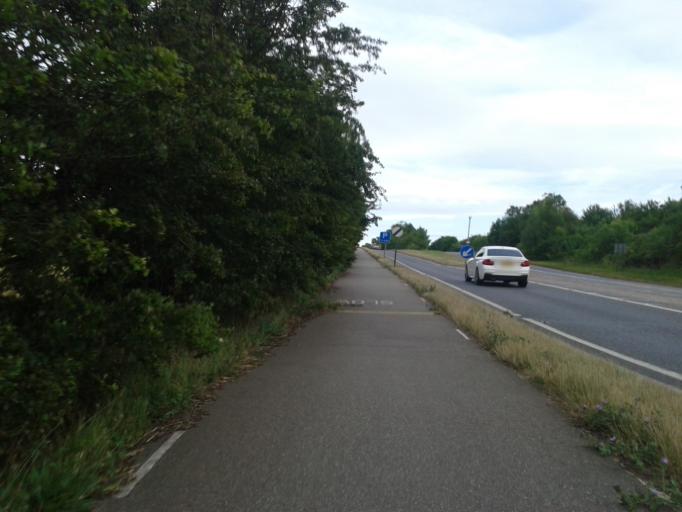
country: GB
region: England
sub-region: Cambridgeshire
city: Sawston
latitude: 52.1595
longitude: 0.1743
